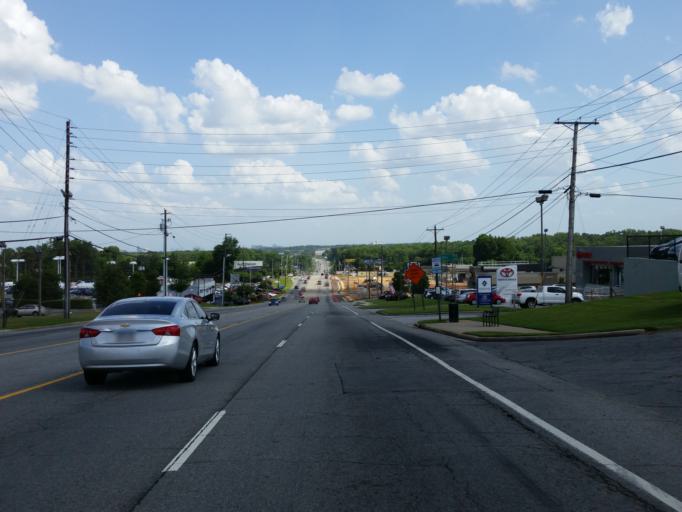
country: US
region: Georgia
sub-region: Cobb County
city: Fair Oaks
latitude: 33.9352
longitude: -84.5122
